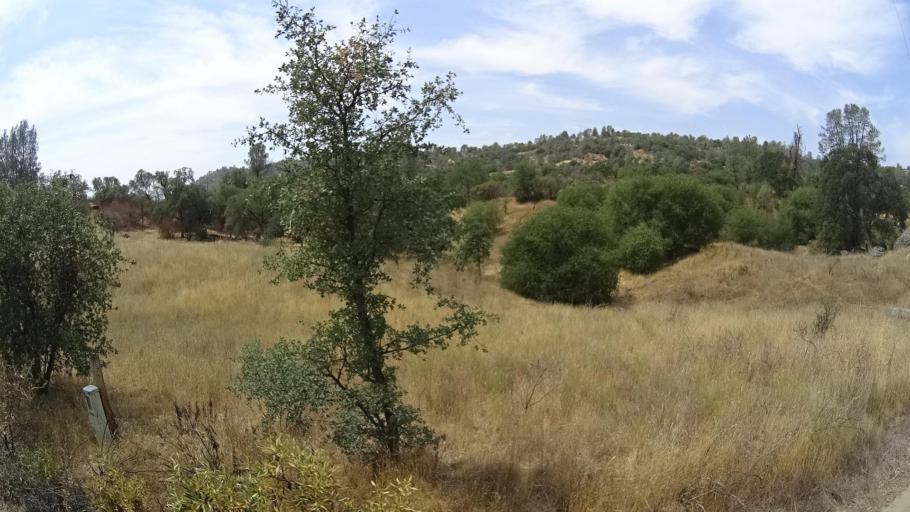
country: US
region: California
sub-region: Madera County
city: Ahwahnee
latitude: 37.3969
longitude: -119.8405
